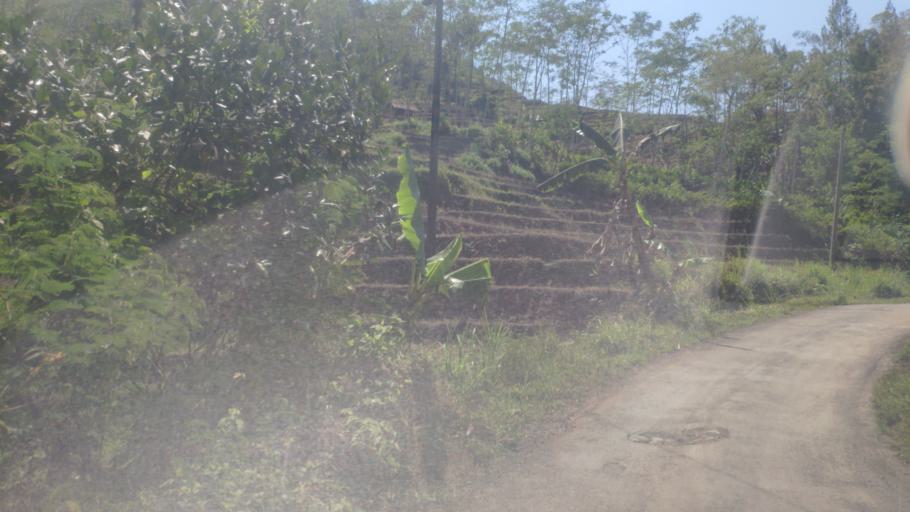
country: ID
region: Central Java
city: Buaran
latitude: -7.2552
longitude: 109.6014
